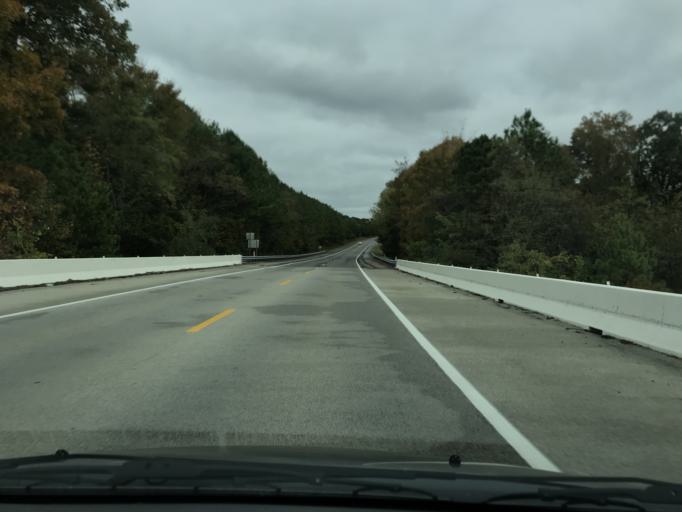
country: US
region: Tennessee
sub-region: Rhea County
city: Graysville
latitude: 35.4139
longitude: -85.0217
